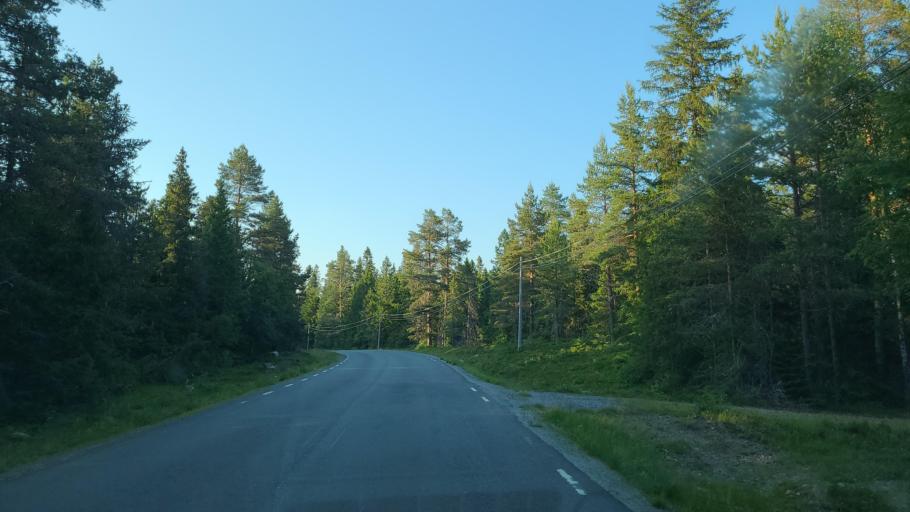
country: SE
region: Vaesterbotten
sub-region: Skelleftea Kommun
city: Burea
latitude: 64.4627
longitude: 21.5865
